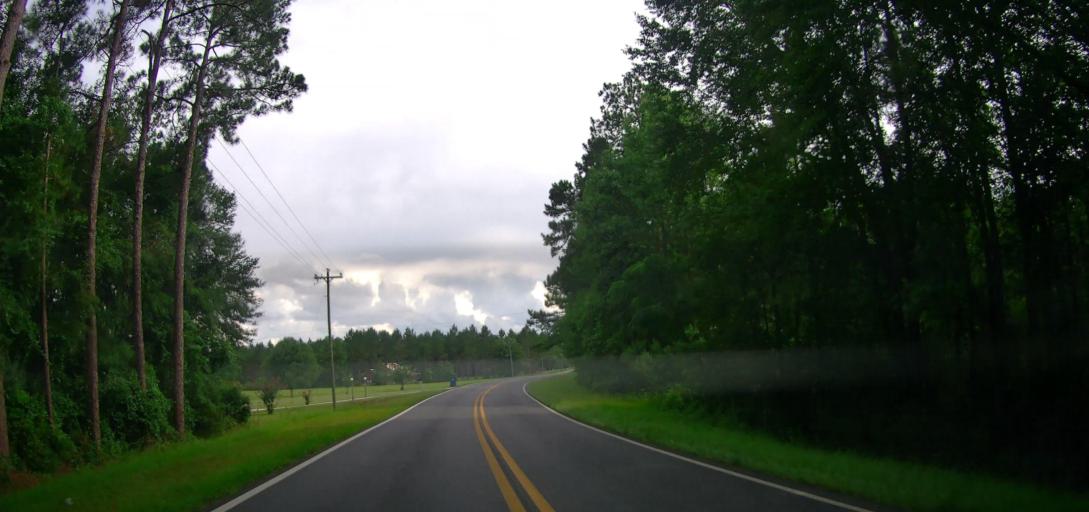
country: US
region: Georgia
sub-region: Wayne County
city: Jesup
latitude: 31.6746
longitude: -81.9180
